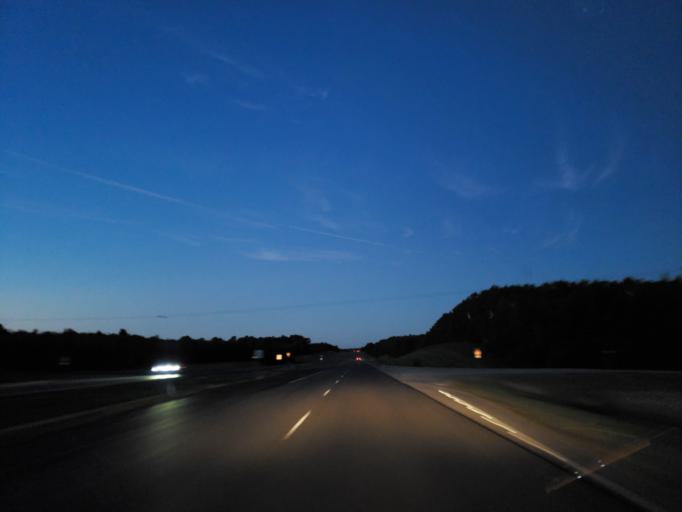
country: US
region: Mississippi
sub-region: Clarke County
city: Quitman
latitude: 32.0119
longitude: -88.6881
